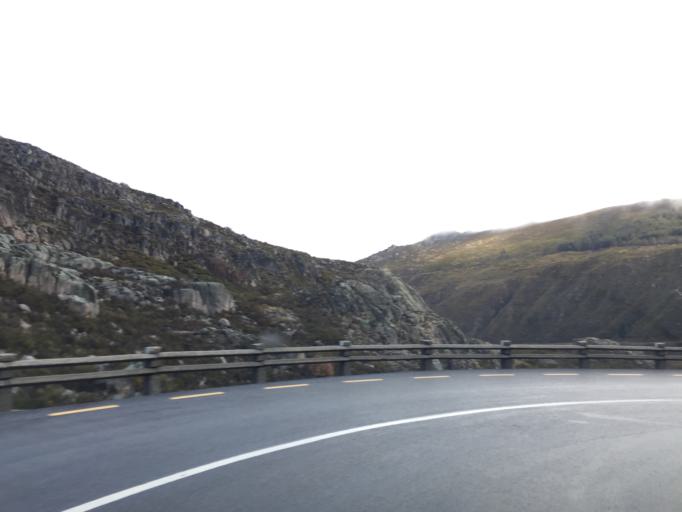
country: PT
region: Guarda
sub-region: Manteigas
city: Manteigas
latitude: 40.3281
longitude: -7.5867
